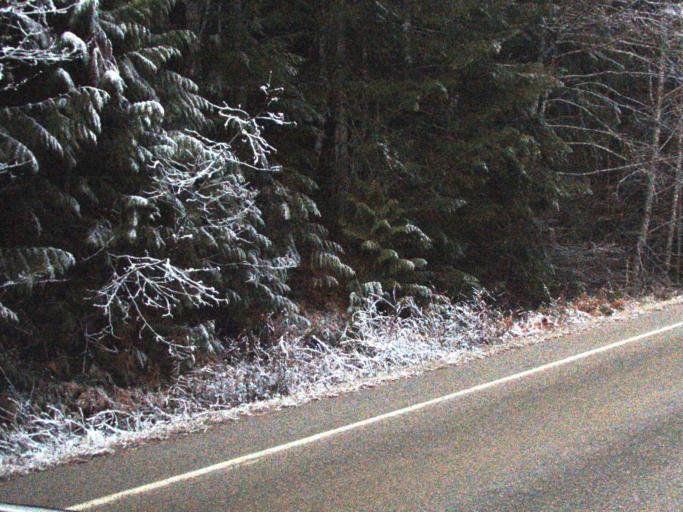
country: US
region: Washington
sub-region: Snohomish County
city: Darrington
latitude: 48.6983
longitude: -121.1100
